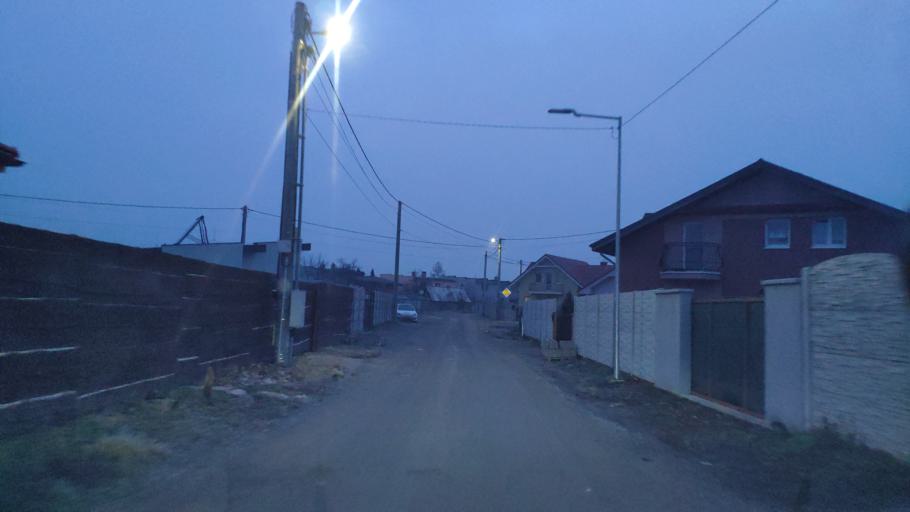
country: SK
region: Kosicky
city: Kosice
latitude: 48.6127
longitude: 21.3307
